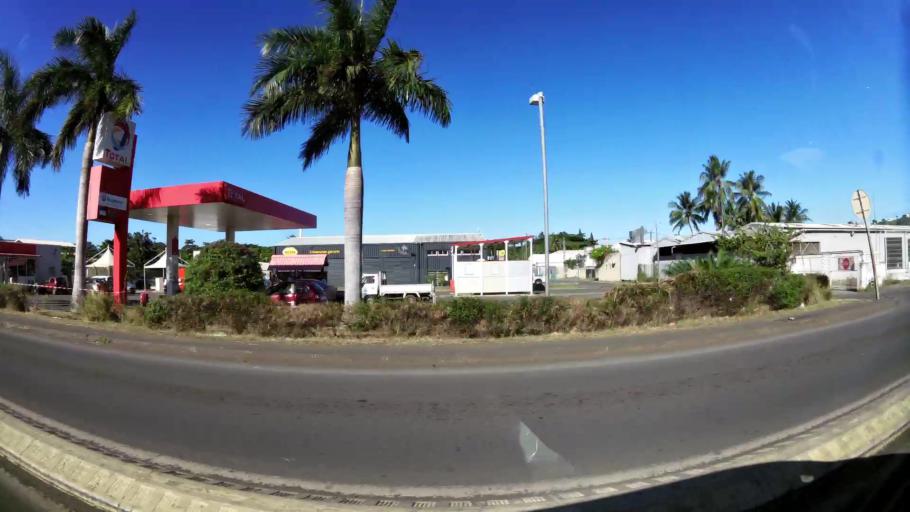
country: YT
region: Mamoudzou
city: Mamoudzou
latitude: -12.7700
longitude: 45.2239
